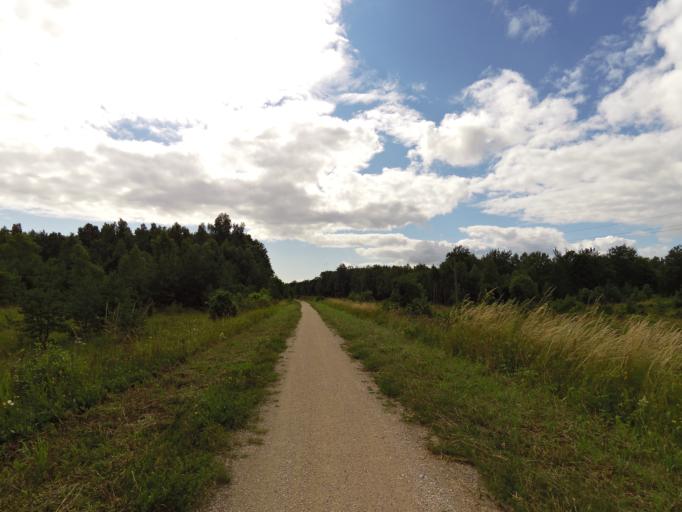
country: EE
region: Laeaene
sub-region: Haapsalu linn
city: Haapsalu
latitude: 58.9184
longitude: 23.4483
